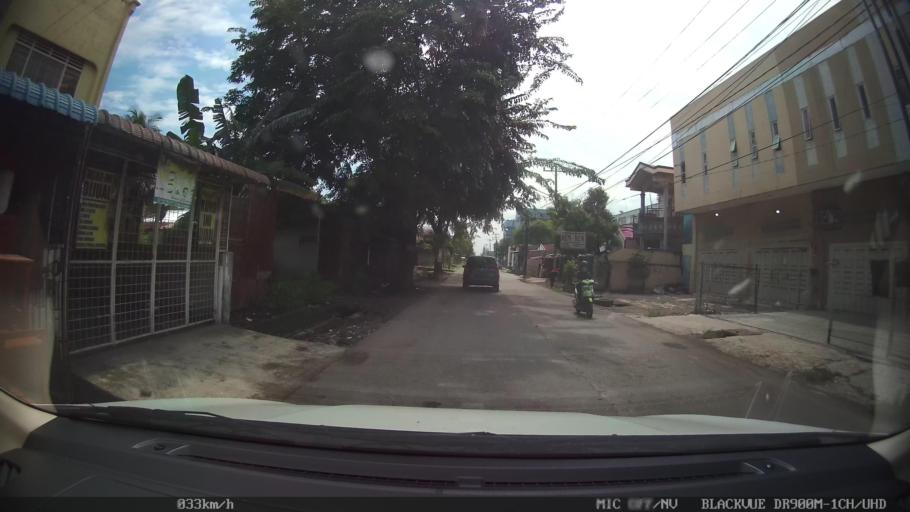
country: ID
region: North Sumatra
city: Medan
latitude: 3.5874
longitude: 98.7145
